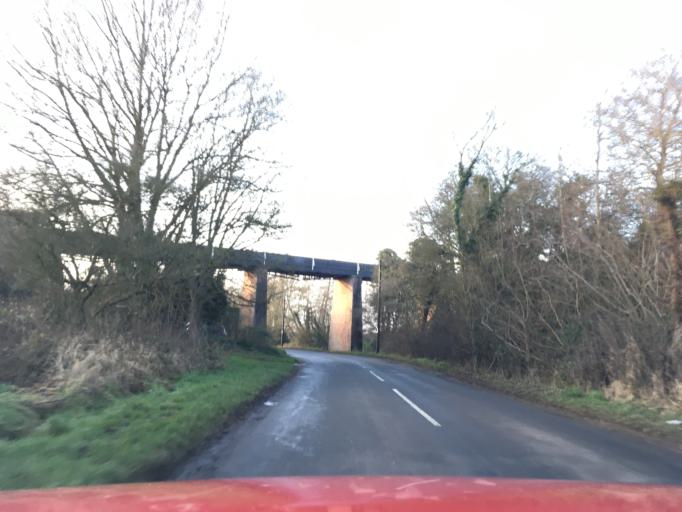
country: GB
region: England
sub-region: Warwickshire
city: Henley in Arden
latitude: 52.2459
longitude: -1.7632
